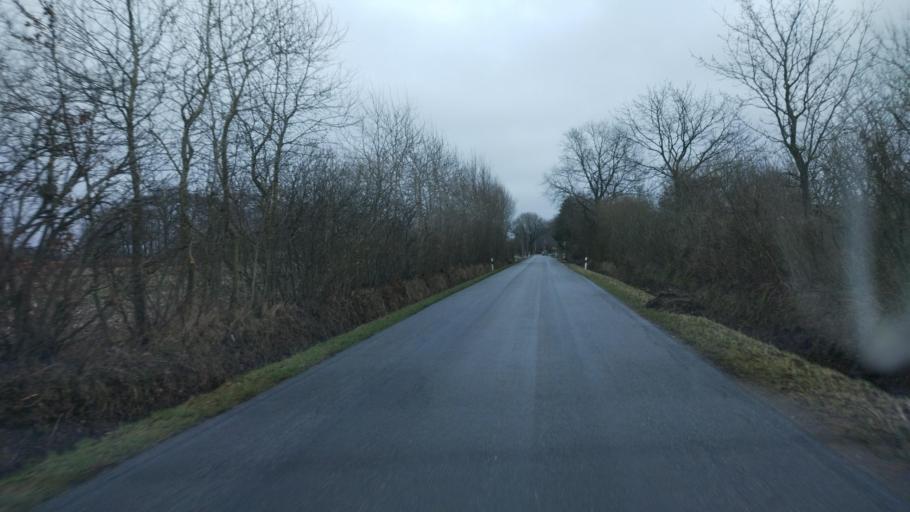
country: DE
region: Schleswig-Holstein
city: Ellingstedt
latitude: 54.4839
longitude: 9.4018
